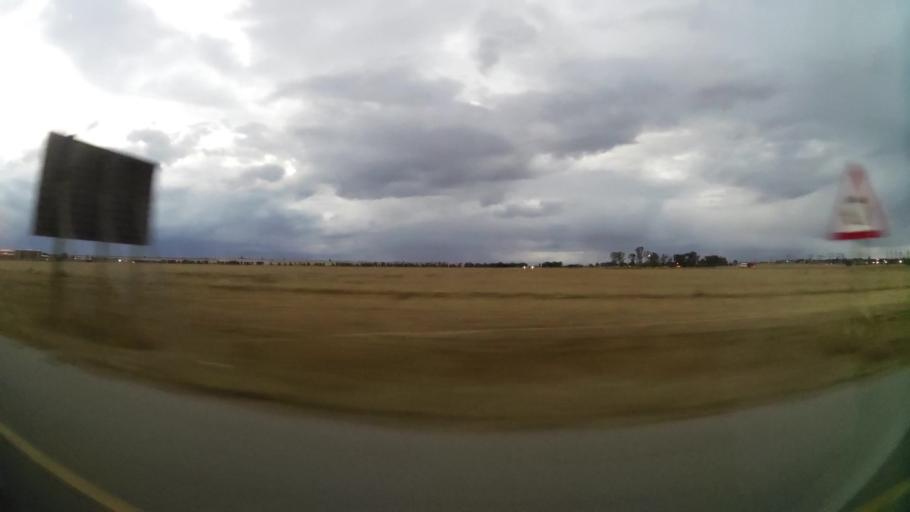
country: ZA
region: Orange Free State
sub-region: Lejweleputswa District Municipality
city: Welkom
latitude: -27.9497
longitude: 26.7951
